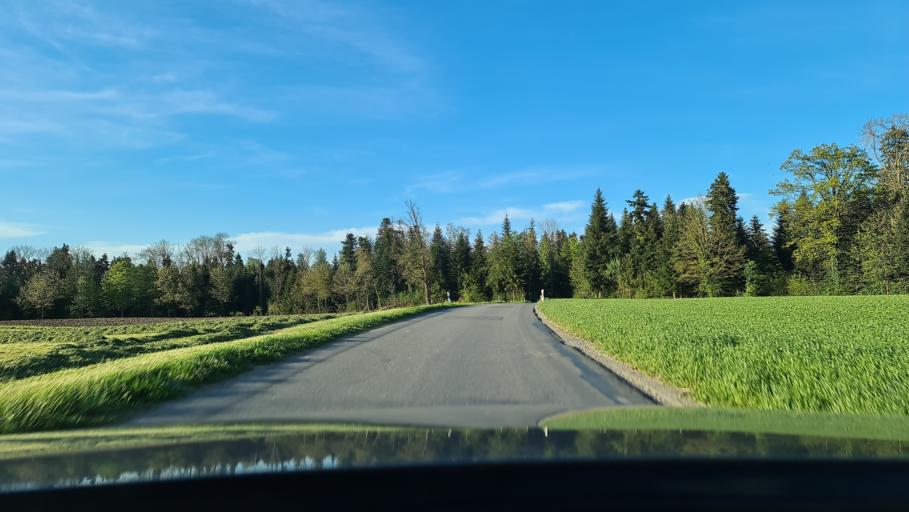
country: CH
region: Lucerne
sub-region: Sursee District
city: Buttisholz
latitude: 47.0854
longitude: 8.0935
